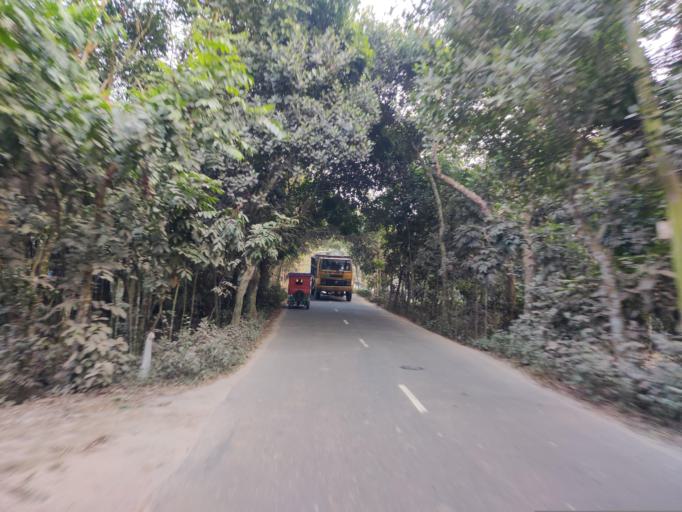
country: BD
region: Dhaka
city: Bajitpur
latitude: 24.1594
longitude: 90.7993
